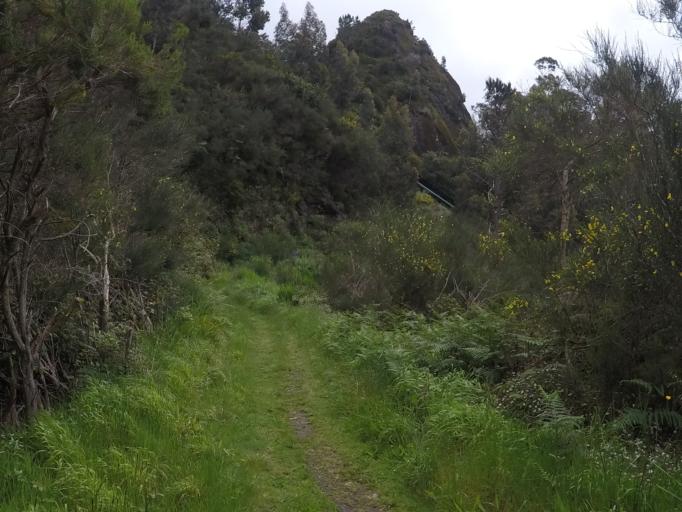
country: PT
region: Madeira
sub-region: Sao Vicente
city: Sao Vicente
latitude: 32.7487
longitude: -17.0170
